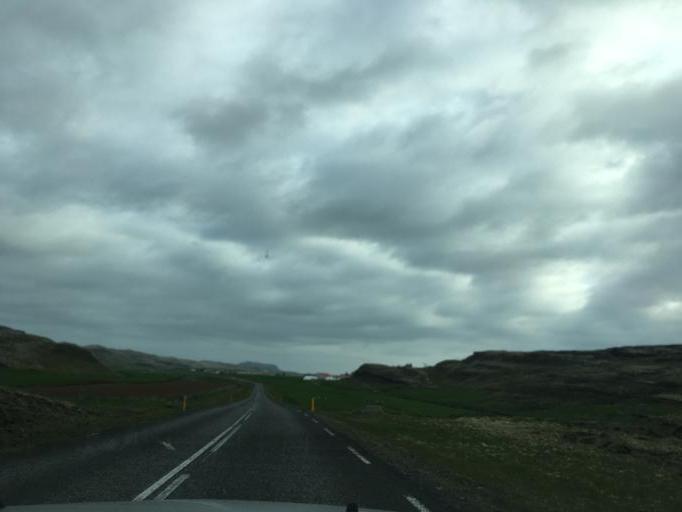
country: IS
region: South
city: Vestmannaeyjar
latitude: 64.2038
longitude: -20.2745
